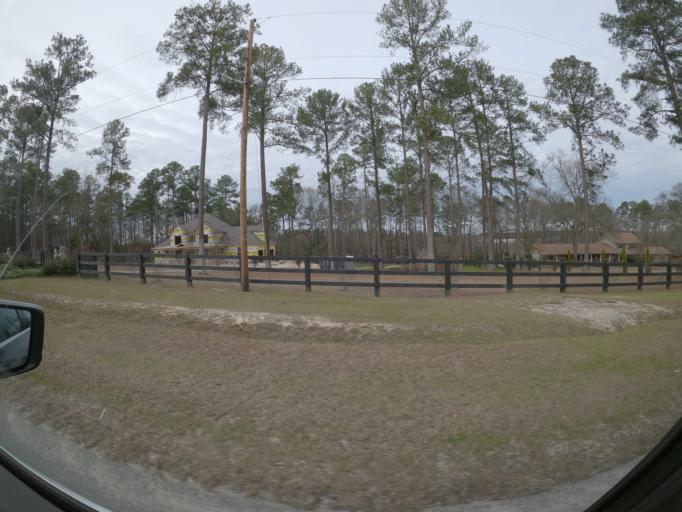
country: US
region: Georgia
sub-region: Columbia County
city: Grovetown
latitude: 33.4627
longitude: -82.1963
